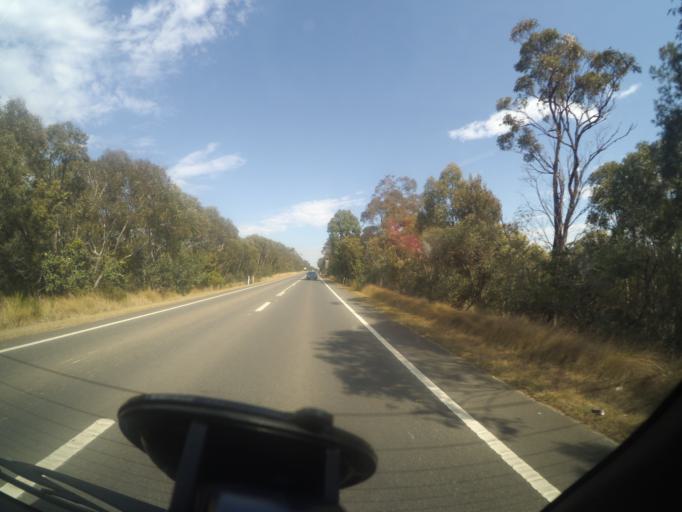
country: AU
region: New South Wales
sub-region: Sutherland Shire
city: Menai
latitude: -34.0127
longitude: 150.9855
